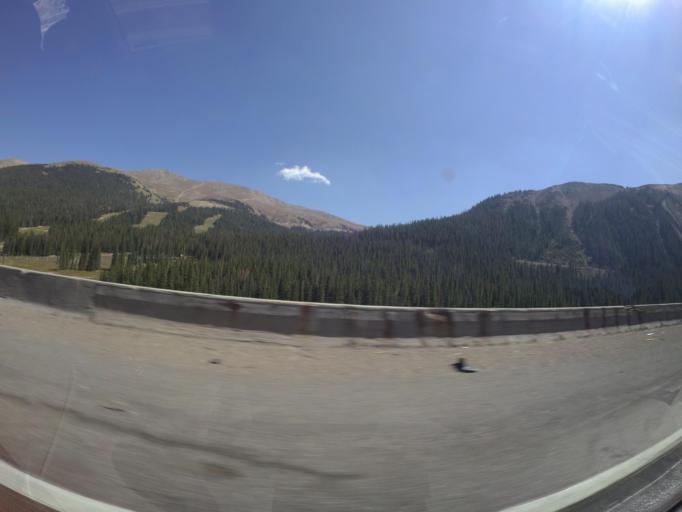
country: US
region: Colorado
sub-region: Summit County
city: Keystone
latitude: 39.6829
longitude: -105.8909
